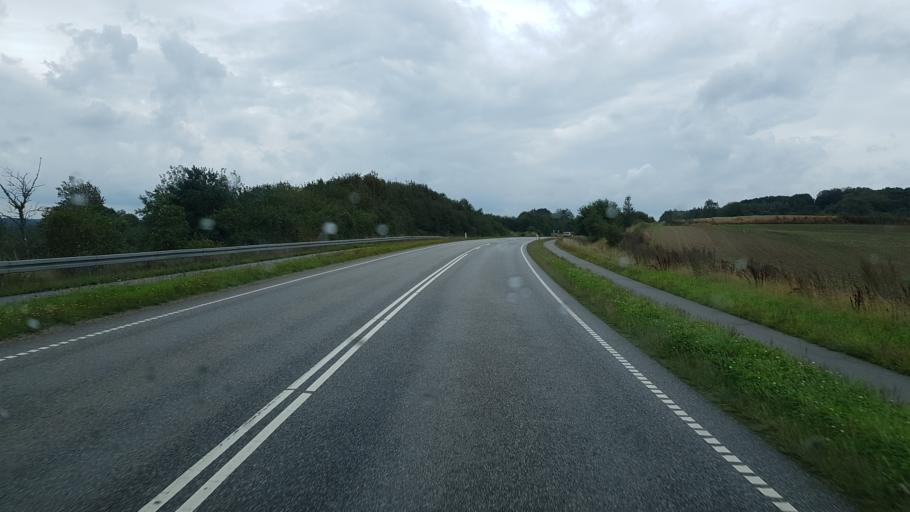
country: DK
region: Central Jutland
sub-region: Horsens Kommune
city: Horsens
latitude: 55.9034
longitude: 9.7436
